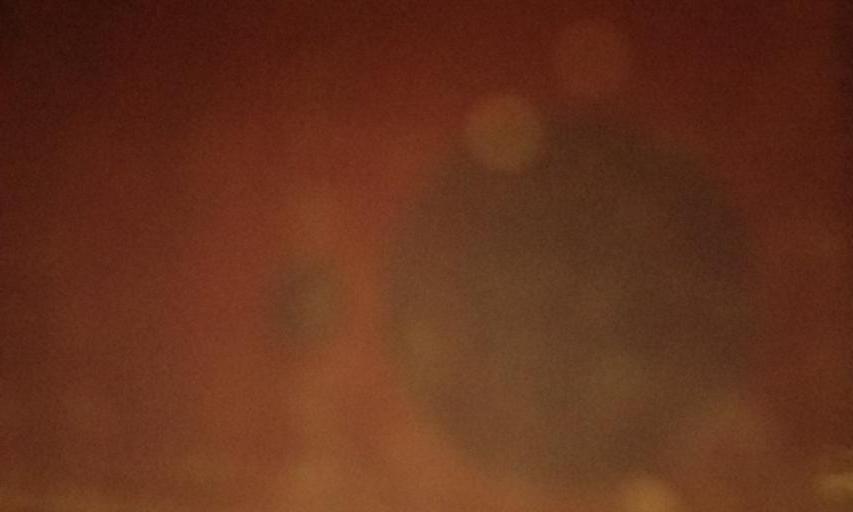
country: JP
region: Hiroshima
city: Onomichi
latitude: 34.4239
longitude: 133.1714
